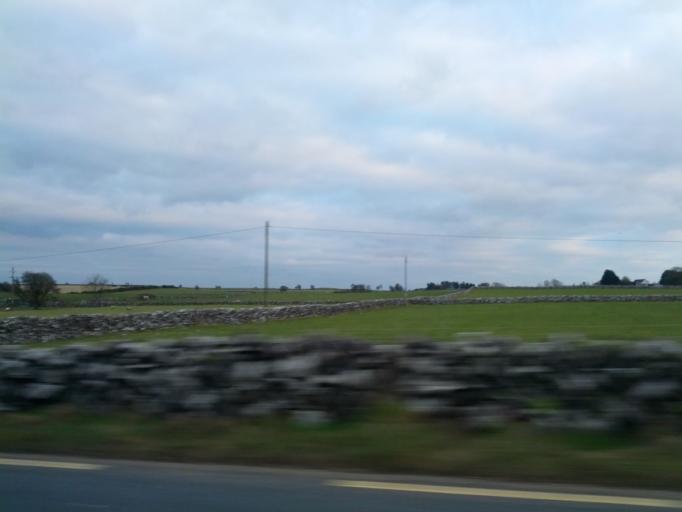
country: IE
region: Connaught
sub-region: County Galway
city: Claregalway
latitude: 53.3947
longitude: -8.8380
